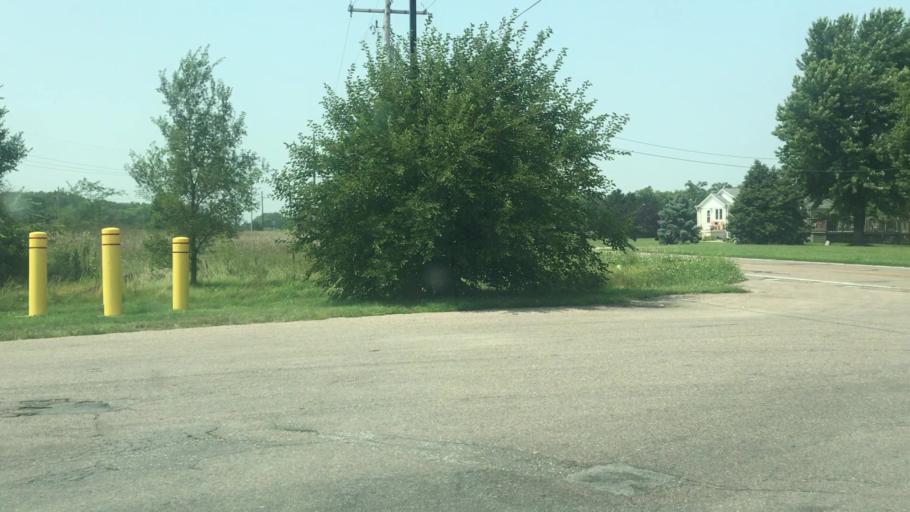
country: US
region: Nebraska
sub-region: Hall County
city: Grand Island
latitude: 40.9157
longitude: -98.3028
